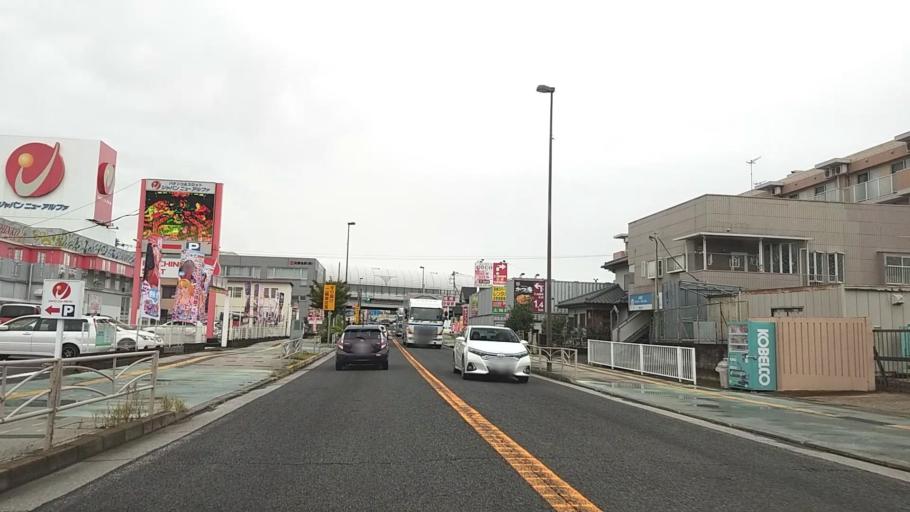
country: JP
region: Kanagawa
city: Atsugi
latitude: 35.4239
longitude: 139.3494
